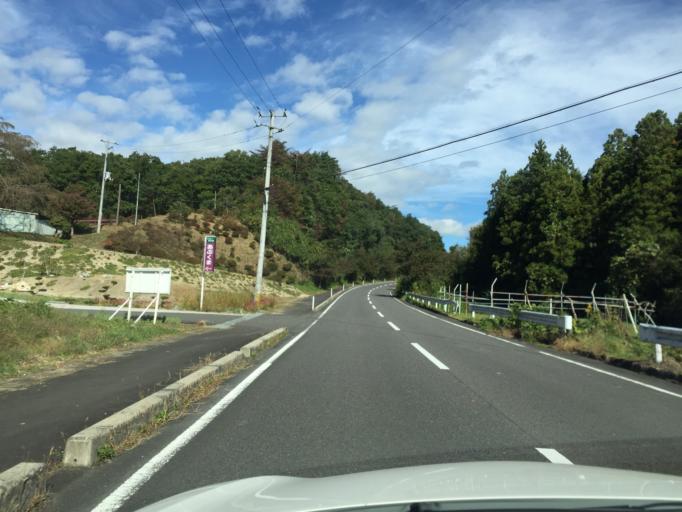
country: JP
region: Fukushima
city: Miharu
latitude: 37.4296
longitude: 140.5237
